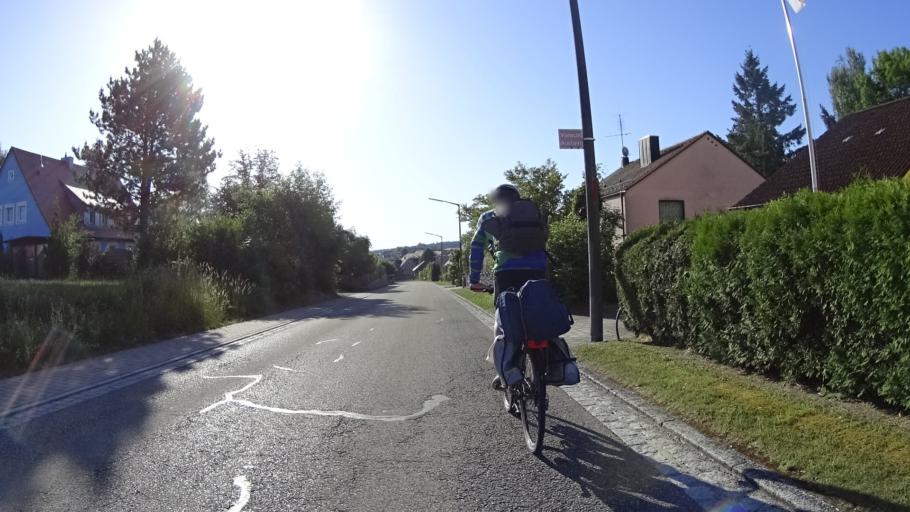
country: DE
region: Bavaria
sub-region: Regierungsbezirk Mittelfranken
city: Dentlein am Forst
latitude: 49.1484
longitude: 10.4168
